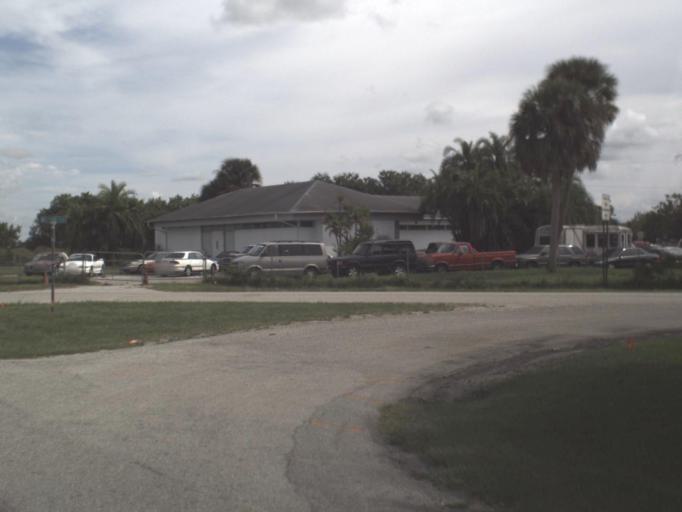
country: US
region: Florida
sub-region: Okeechobee County
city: Taylor Creek
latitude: 27.2612
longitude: -80.7438
